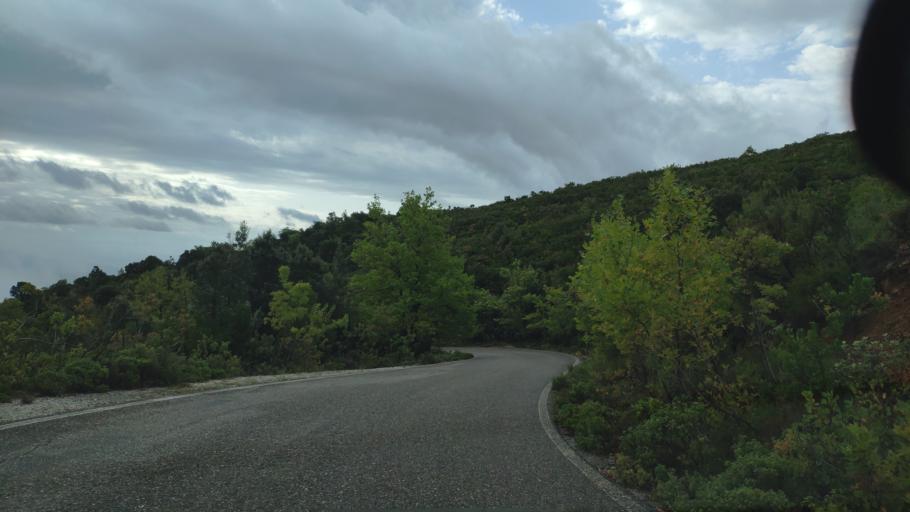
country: GR
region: West Greece
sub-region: Nomos Aitolias kai Akarnanias
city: Sardinia
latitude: 38.8554
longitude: 21.3120
